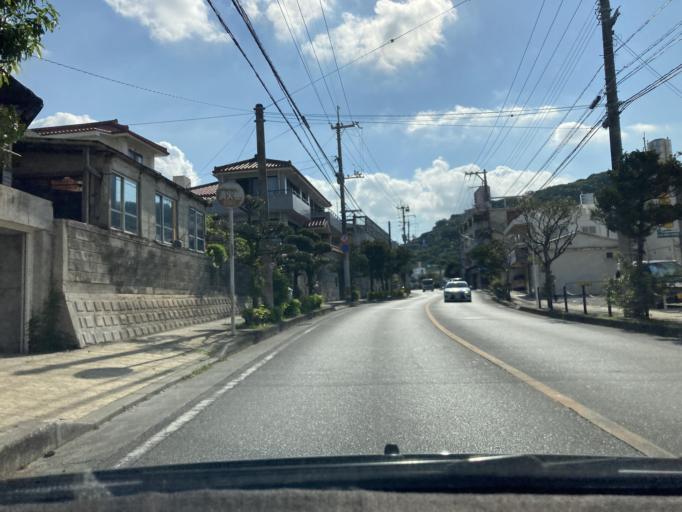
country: JP
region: Okinawa
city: Naha-shi
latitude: 26.2151
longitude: 127.7130
